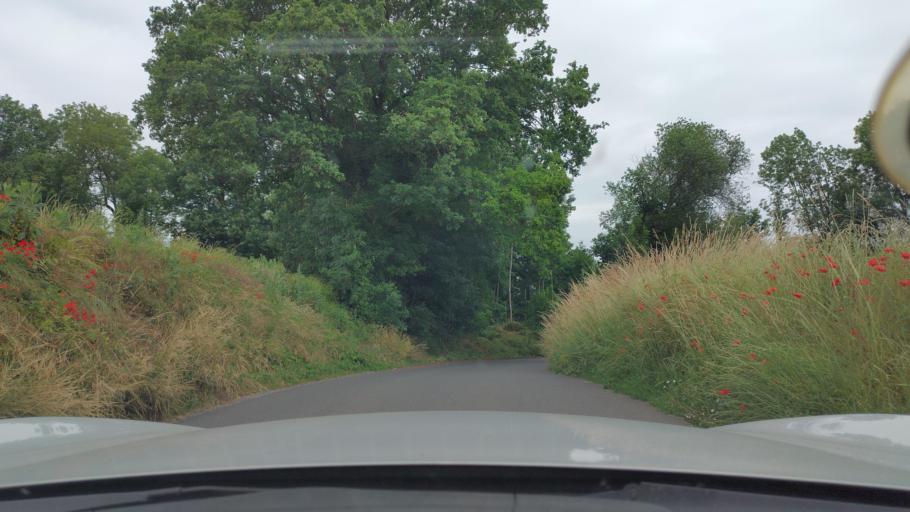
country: FR
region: Picardie
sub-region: Departement de l'Oise
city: Betz
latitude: 49.1511
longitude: 2.9609
